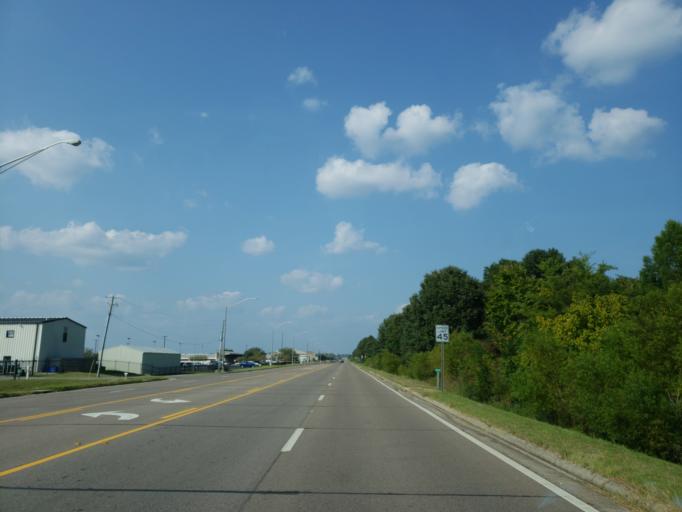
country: US
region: Mississippi
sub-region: Lauderdale County
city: Meridian
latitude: 32.3309
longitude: -88.7456
